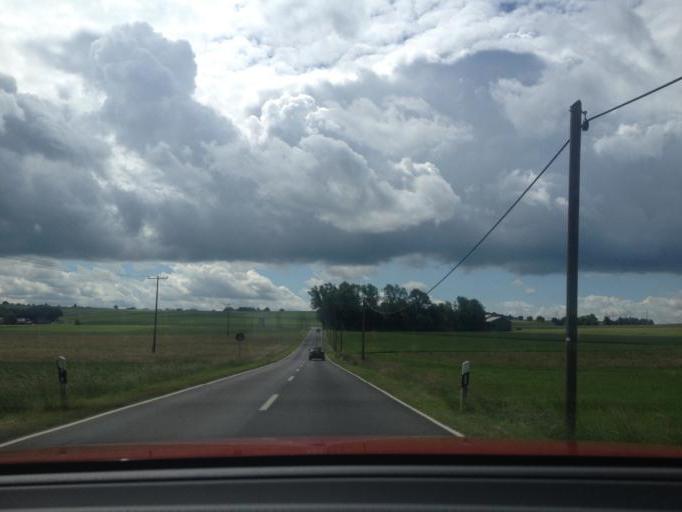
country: DE
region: Bavaria
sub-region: Upper Franconia
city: Arzberg
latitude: 50.0270
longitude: 12.2039
